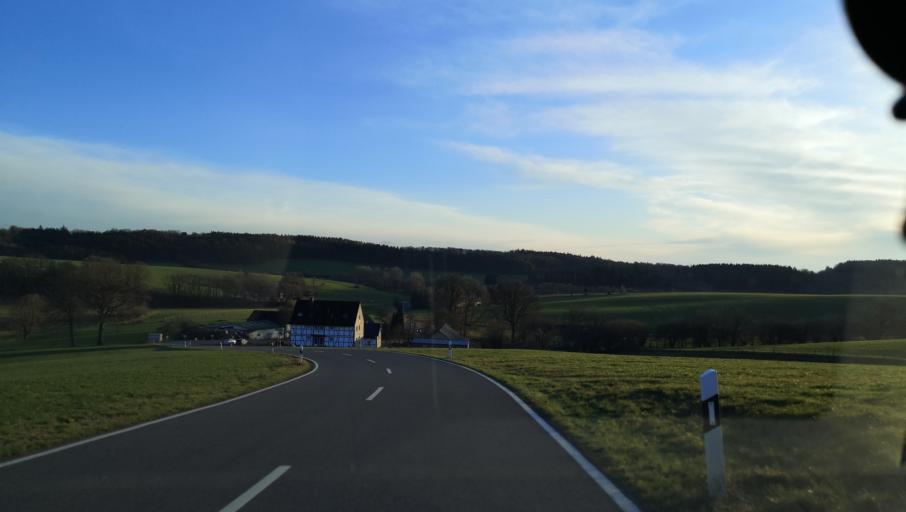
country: DE
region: North Rhine-Westphalia
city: Radevormwald
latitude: 51.1805
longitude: 7.3951
